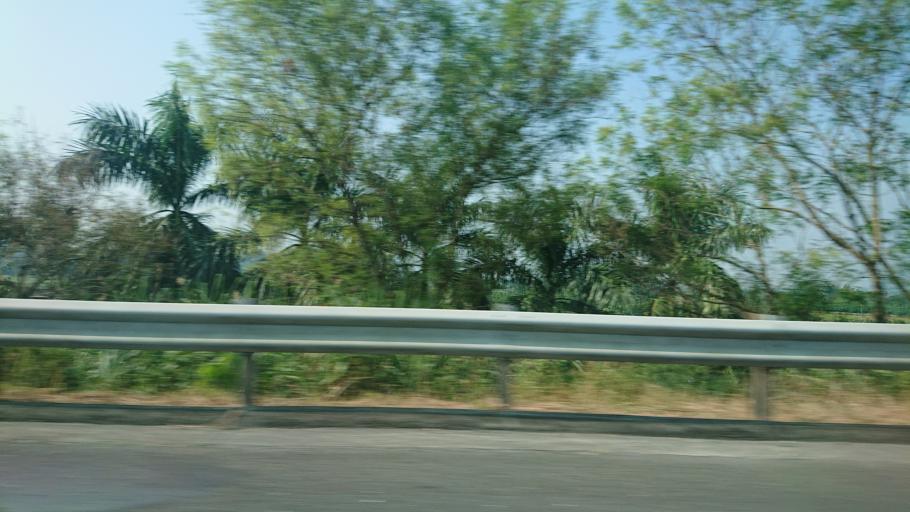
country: TW
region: Taiwan
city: Lugu
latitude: 23.7934
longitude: 120.7030
